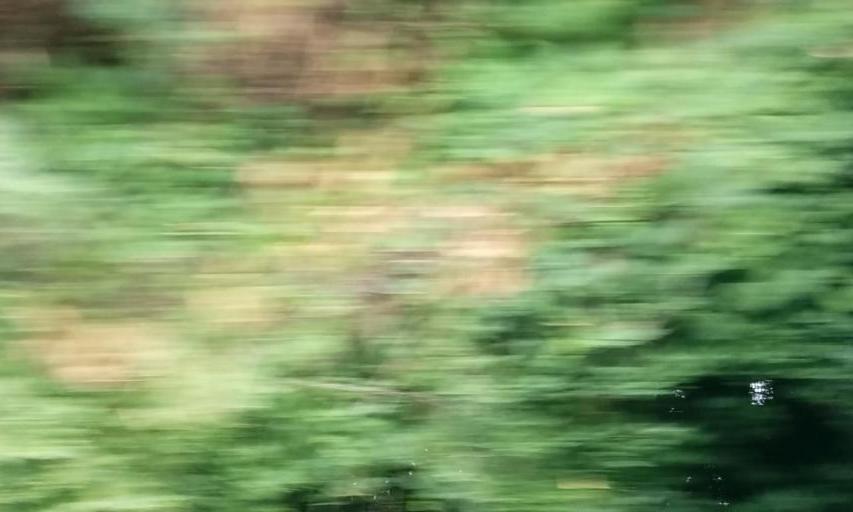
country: JP
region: Chiba
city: Nagareyama
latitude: 35.8430
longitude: 139.9088
